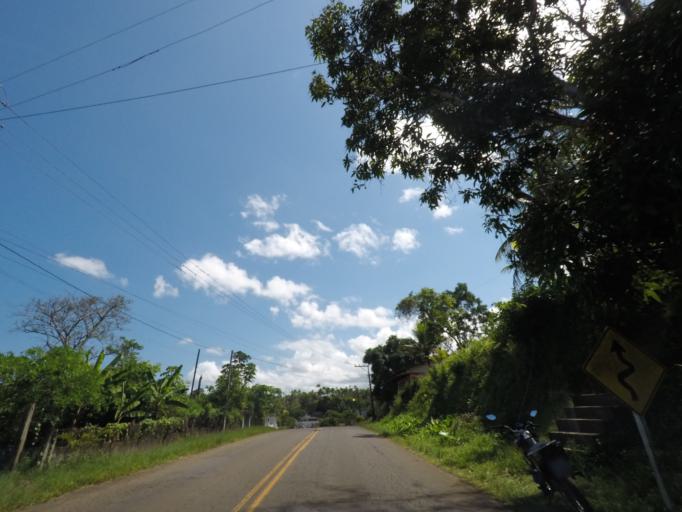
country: BR
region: Bahia
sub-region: Taperoa
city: Taperoa
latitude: -13.4991
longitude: -39.0970
